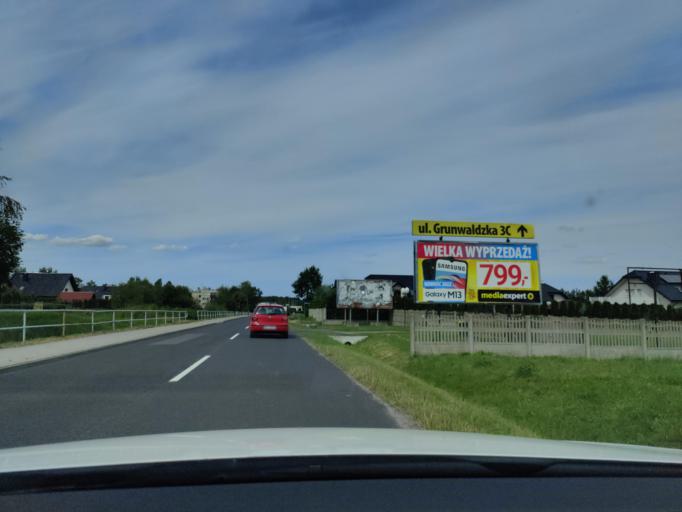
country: PL
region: Opole Voivodeship
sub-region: Powiat nyski
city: Glucholazy
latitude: 50.3031
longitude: 17.3910
